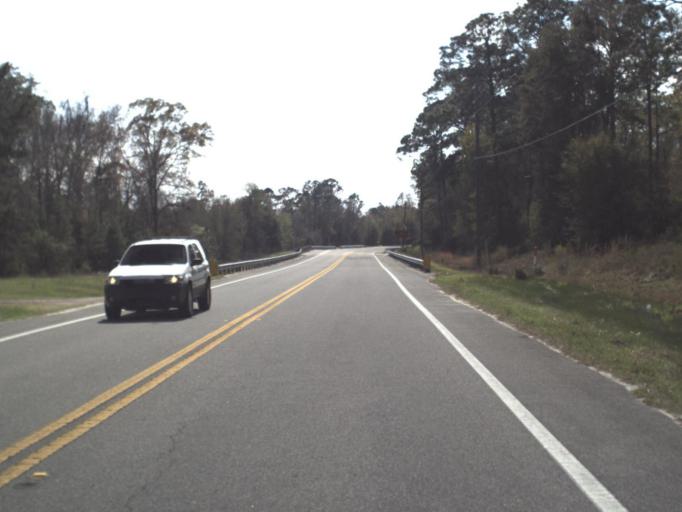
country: US
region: Florida
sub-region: Wakulla County
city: Crawfordville
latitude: 30.0699
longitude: -84.4500
